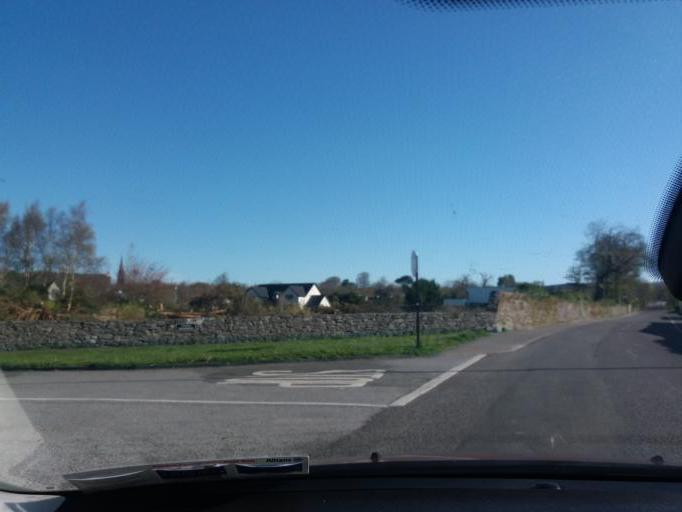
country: IE
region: Munster
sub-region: Ciarrai
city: Cill Airne
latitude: 52.0510
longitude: -9.5170
